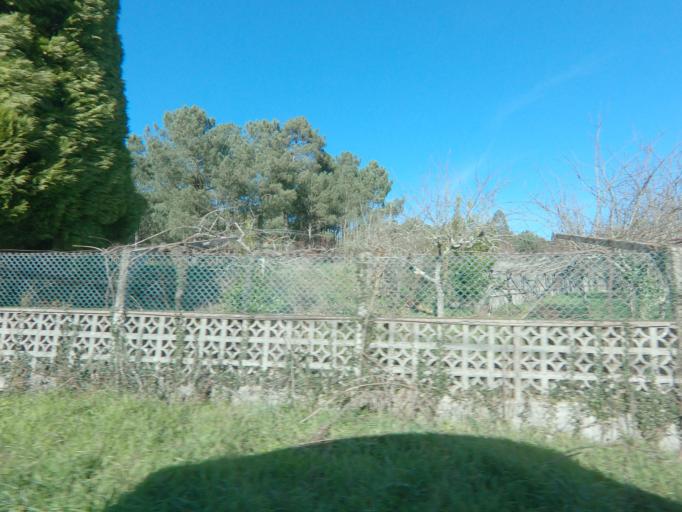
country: ES
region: Galicia
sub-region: Provincia da Coruna
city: Ribeira
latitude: 42.7159
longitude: -8.4378
